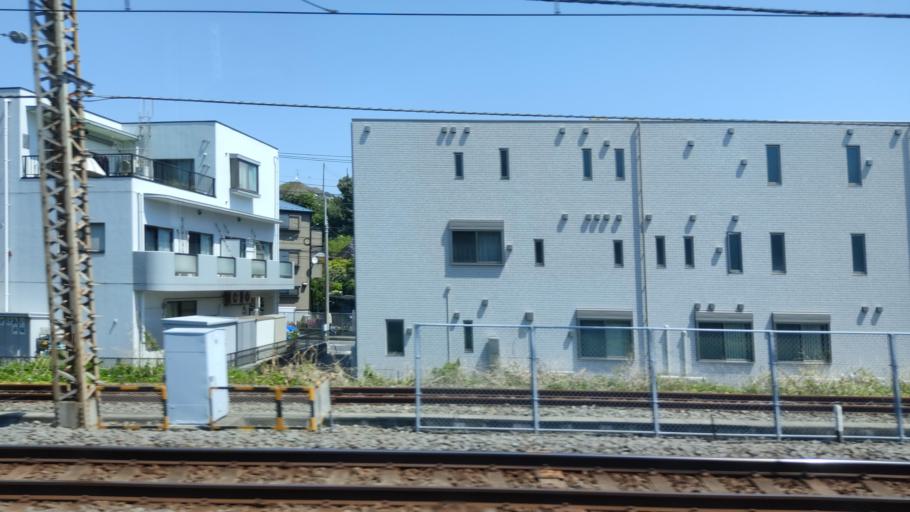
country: JP
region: Kanagawa
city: Fujisawa
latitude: 35.3961
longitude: 139.5357
